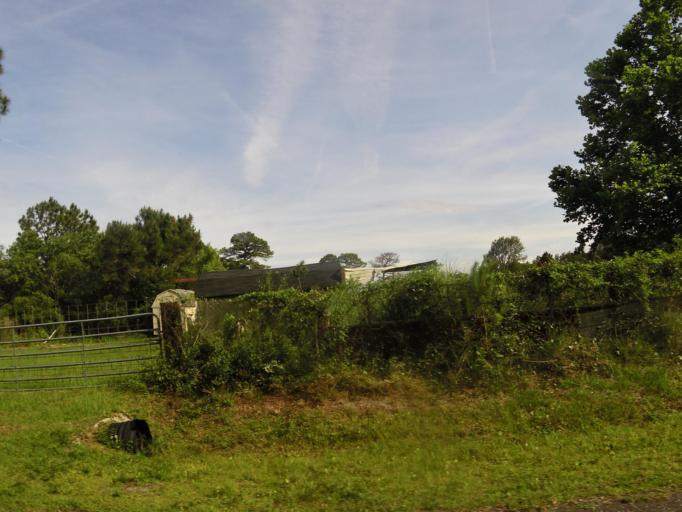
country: US
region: Florida
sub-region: Nassau County
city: Fernandina Beach
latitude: 30.5316
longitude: -81.4874
